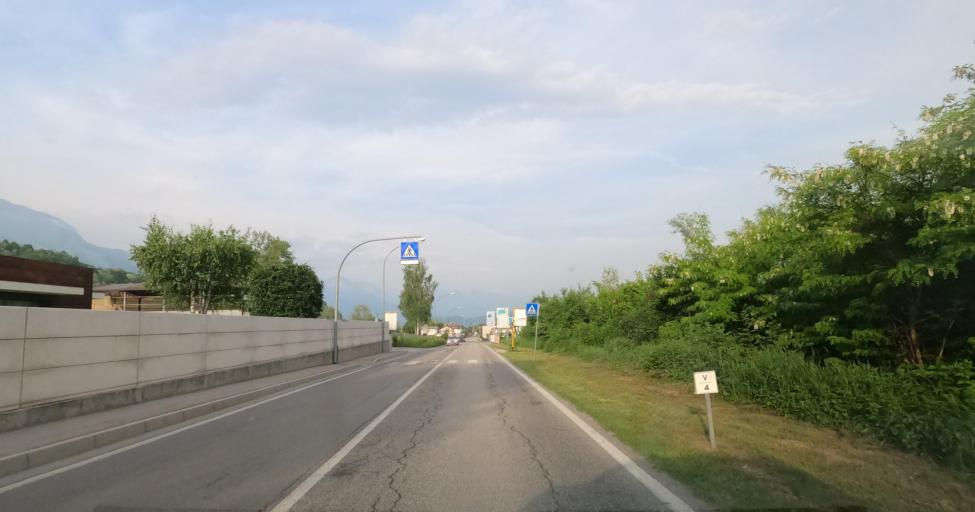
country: IT
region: Veneto
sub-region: Provincia di Belluno
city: Belluno
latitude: 46.1402
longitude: 12.1797
